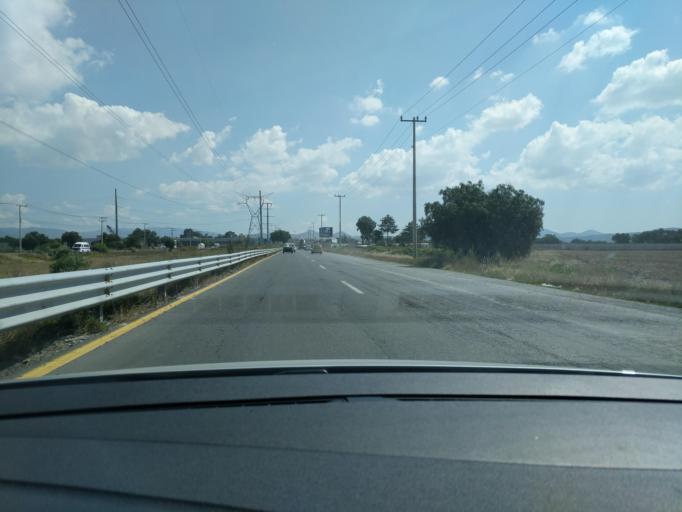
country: MX
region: Hidalgo
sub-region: Mineral de la Reforma
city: Los Tuzos
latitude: 20.0366
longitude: -98.7367
